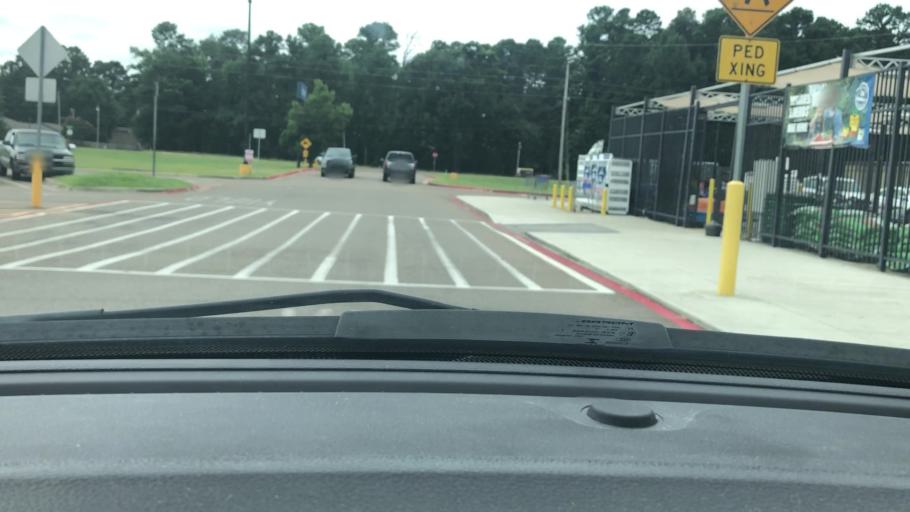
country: US
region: Texas
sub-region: Bowie County
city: Wake Village
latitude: 33.4446
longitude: -94.1006
